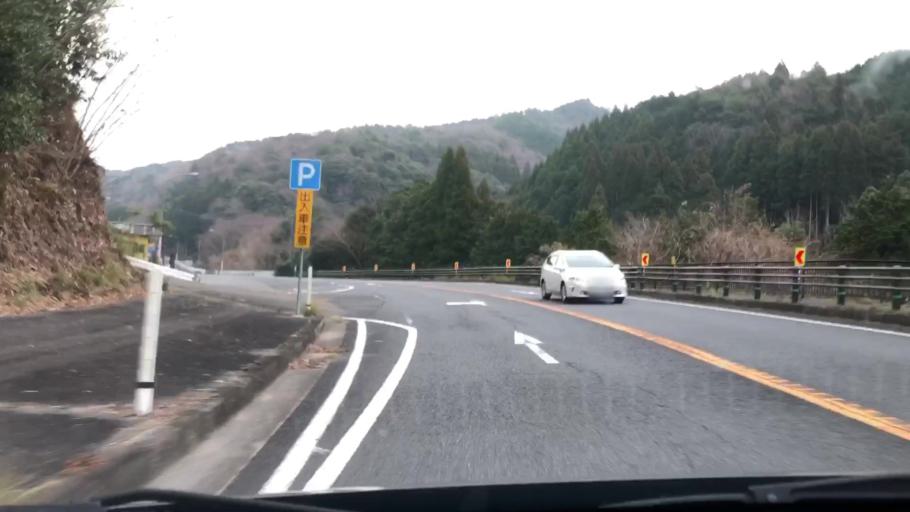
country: JP
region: Oita
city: Usuki
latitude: 32.9957
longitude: 131.7599
